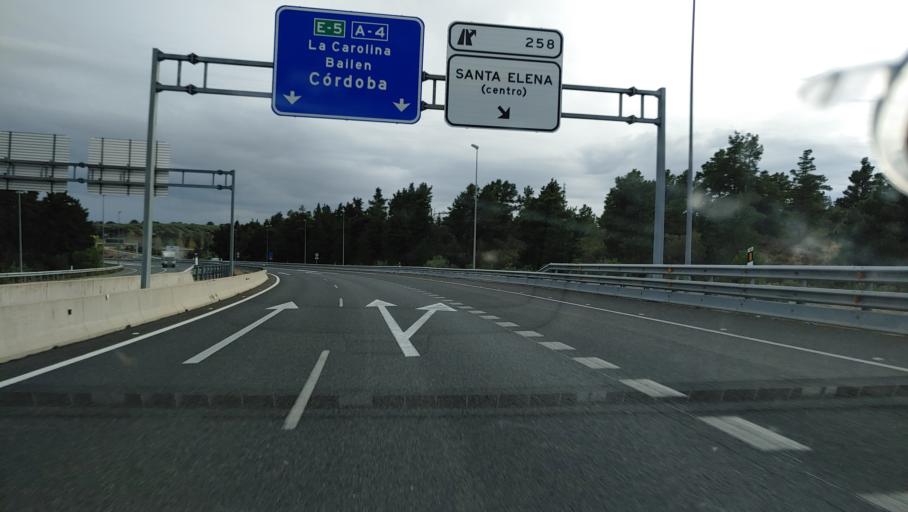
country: ES
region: Andalusia
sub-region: Provincia de Jaen
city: Santa Elena
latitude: 38.3421
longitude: -3.5448
